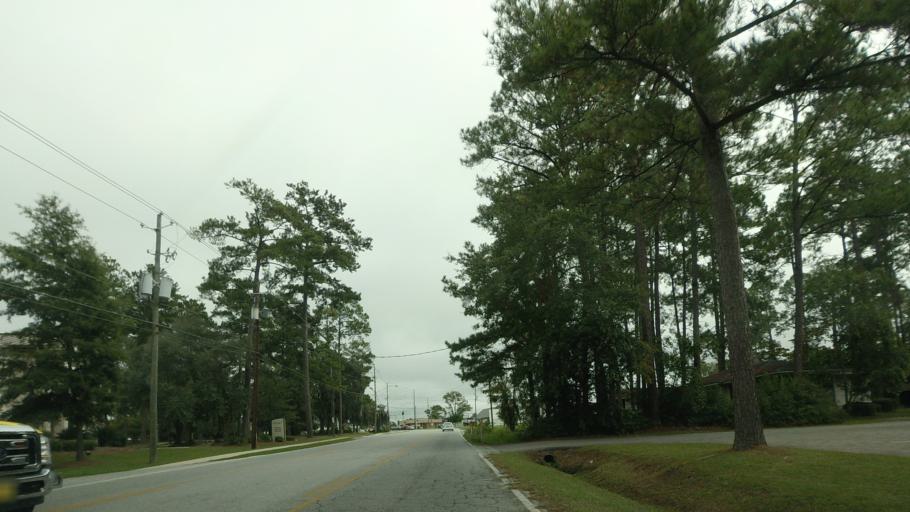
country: US
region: Georgia
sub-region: Lowndes County
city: Valdosta
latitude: 30.8597
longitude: -83.2843
